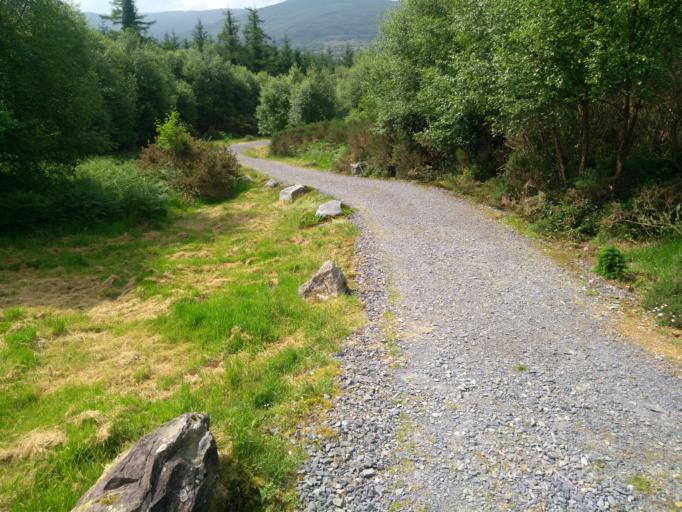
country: IE
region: Munster
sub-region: Ciarrai
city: Kenmare
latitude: 51.8311
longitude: -9.5133
